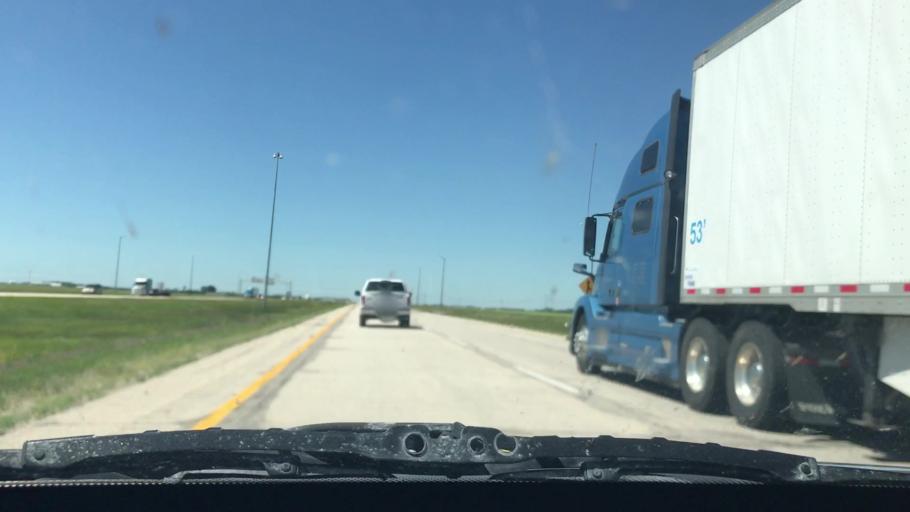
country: CA
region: Manitoba
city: Steinbach
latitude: 49.7027
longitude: -96.6496
